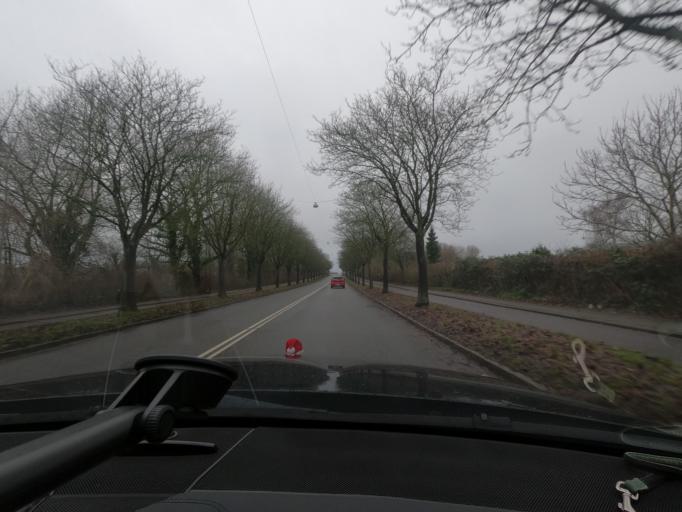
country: DK
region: South Denmark
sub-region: Sonderborg Kommune
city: Sonderborg
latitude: 54.9069
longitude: 9.8220
